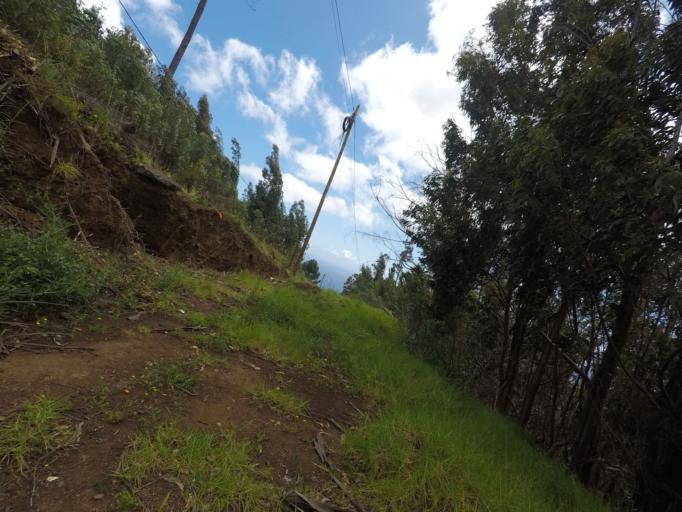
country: PT
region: Madeira
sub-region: Calheta
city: Estreito da Calheta
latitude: 32.7451
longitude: -17.1953
